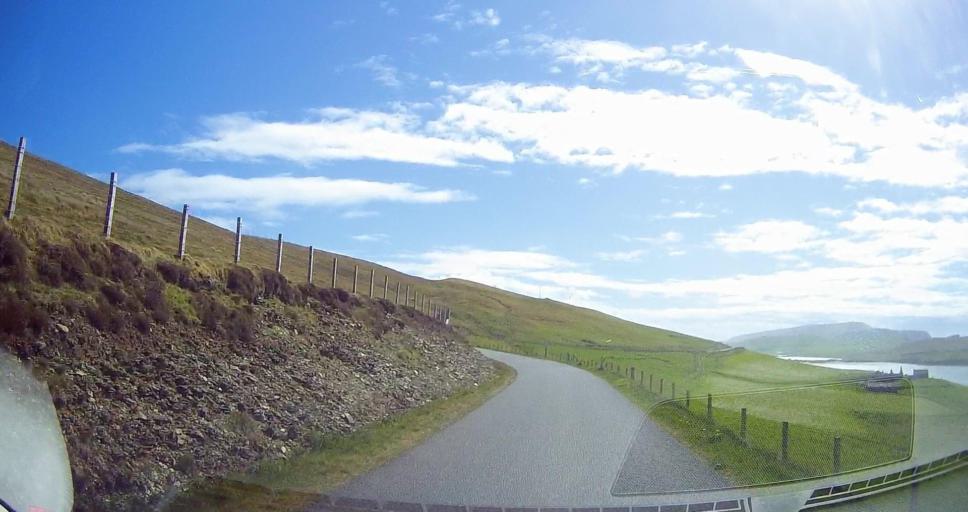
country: GB
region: Scotland
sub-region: Shetland Islands
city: Sandwick
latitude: 59.9575
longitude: -1.3266
